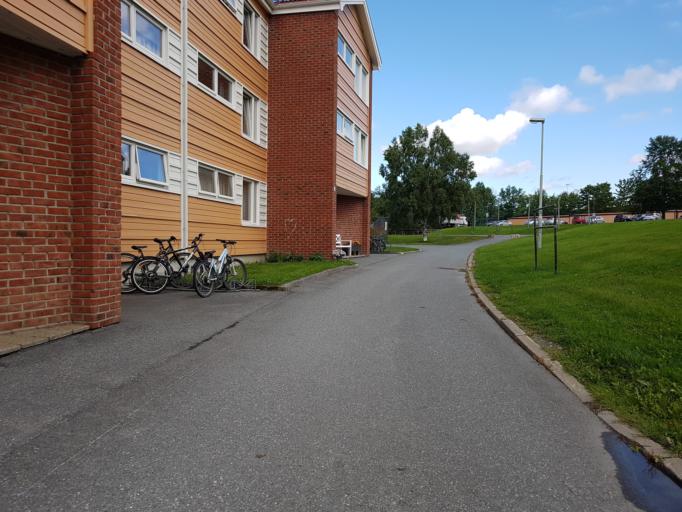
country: NO
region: Sor-Trondelag
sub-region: Trondheim
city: Trondheim
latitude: 63.4161
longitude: 10.4502
